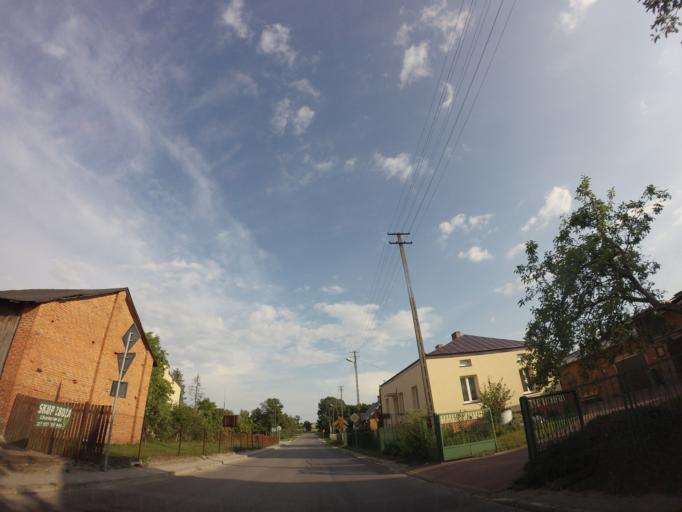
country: PL
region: Lublin Voivodeship
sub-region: Powiat lubartowski
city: Michow
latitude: 51.5215
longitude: 22.3099
